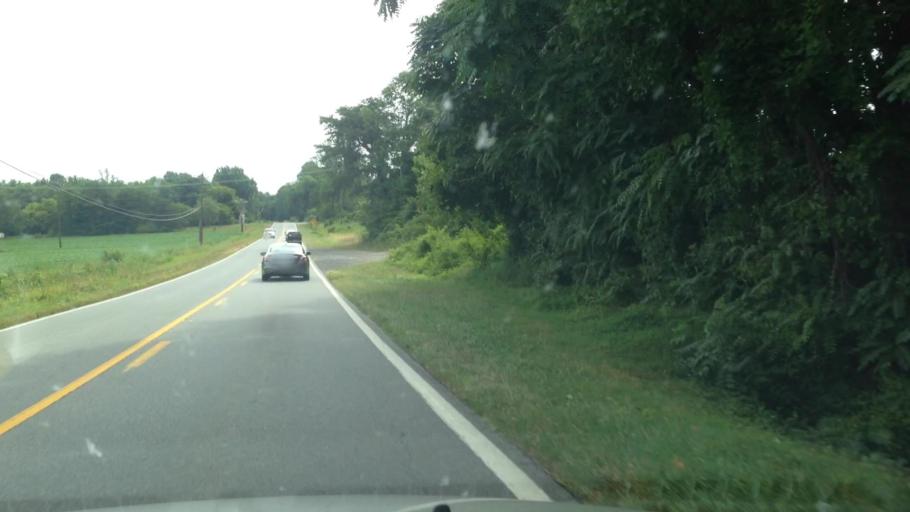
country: US
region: North Carolina
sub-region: Rockingham County
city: Reidsville
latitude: 36.3934
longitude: -79.6383
